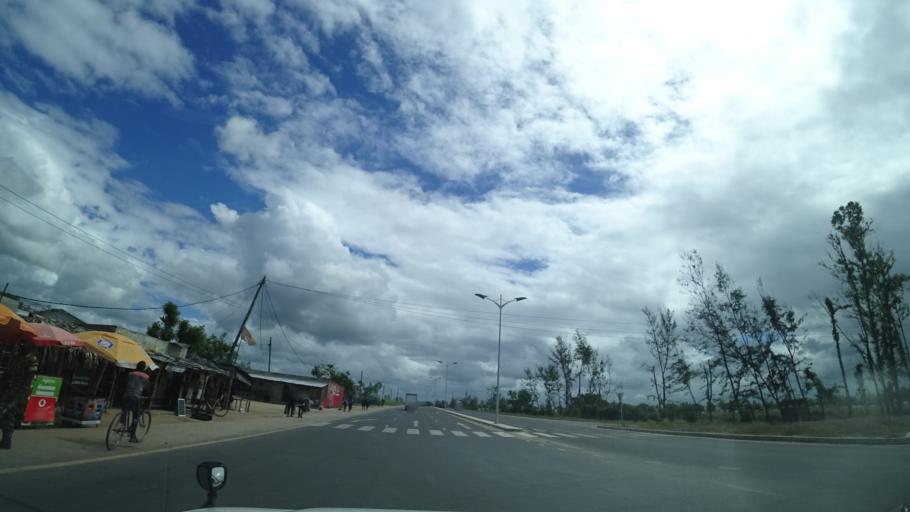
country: MZ
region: Sofala
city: Dondo
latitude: -19.5767
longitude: 34.7226
